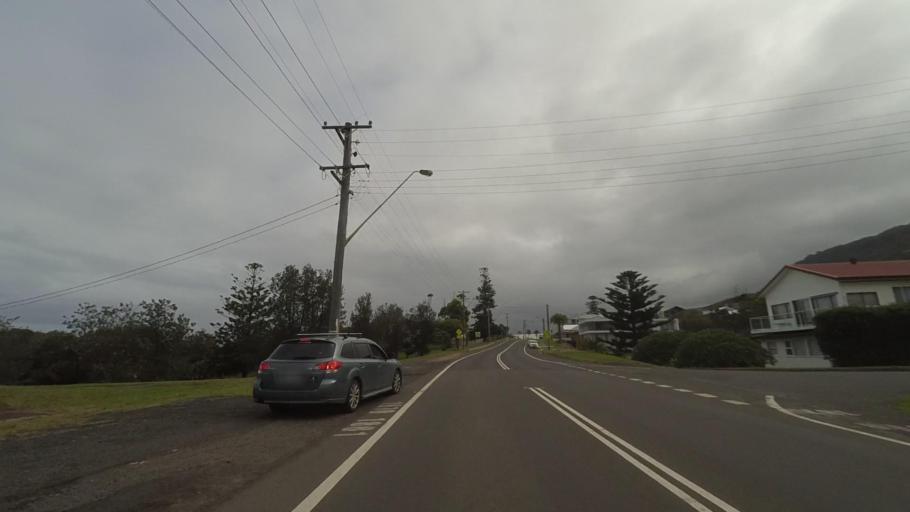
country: AU
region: New South Wales
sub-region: Wollongong
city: Bulli
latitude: -34.2881
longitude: 150.9476
